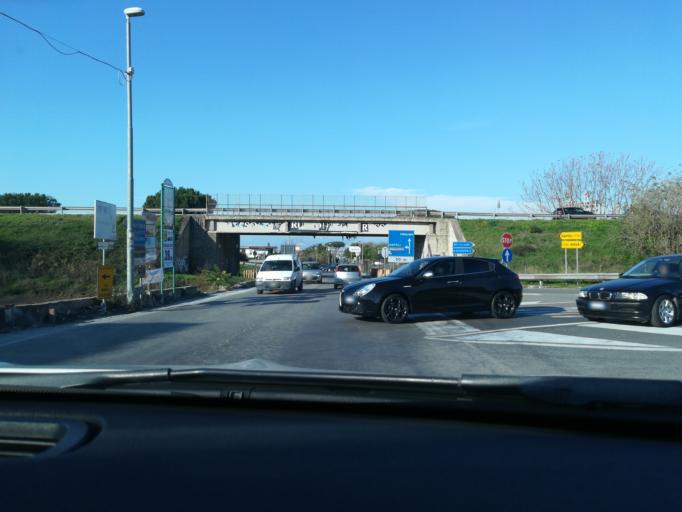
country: IT
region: Campania
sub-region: Provincia di Napoli
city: Sant'Anastasia
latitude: 40.8784
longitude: 14.3990
